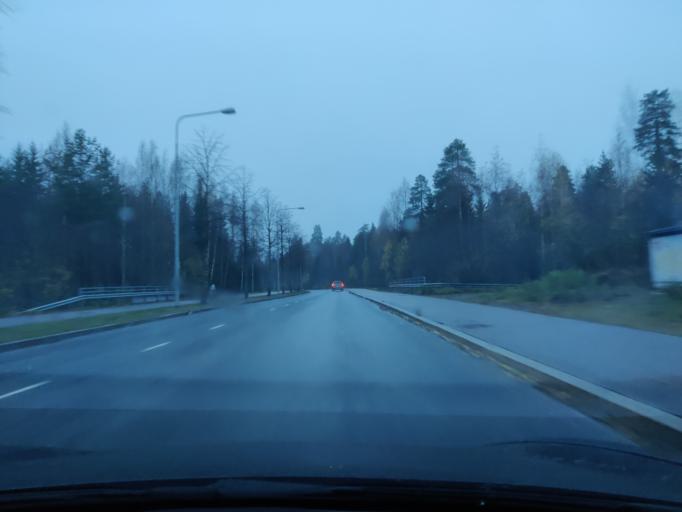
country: FI
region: Northern Savo
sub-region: Kuopio
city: Kuopio
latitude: 62.8293
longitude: 27.6728
